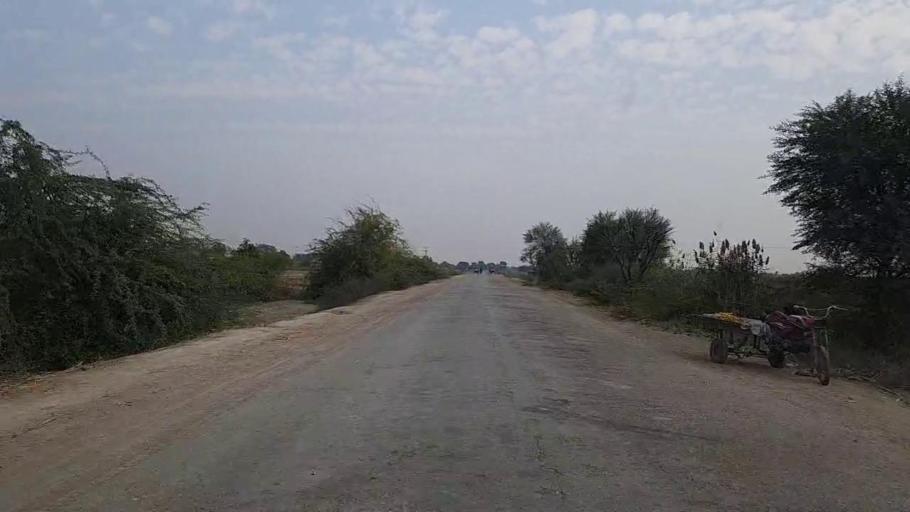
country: PK
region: Sindh
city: Mirwah Gorchani
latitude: 25.4019
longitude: 69.0638
